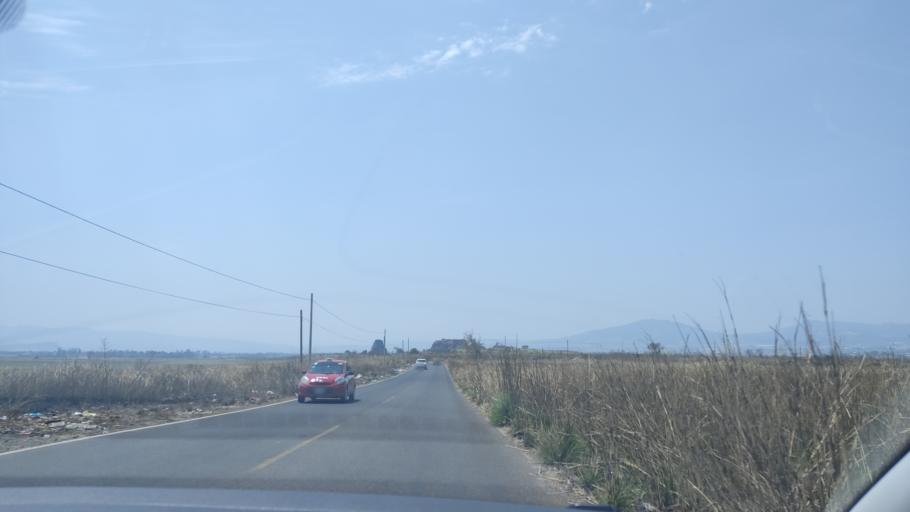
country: MX
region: Nayarit
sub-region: Tepic
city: La Corregidora
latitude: 21.4895
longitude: -104.8042
